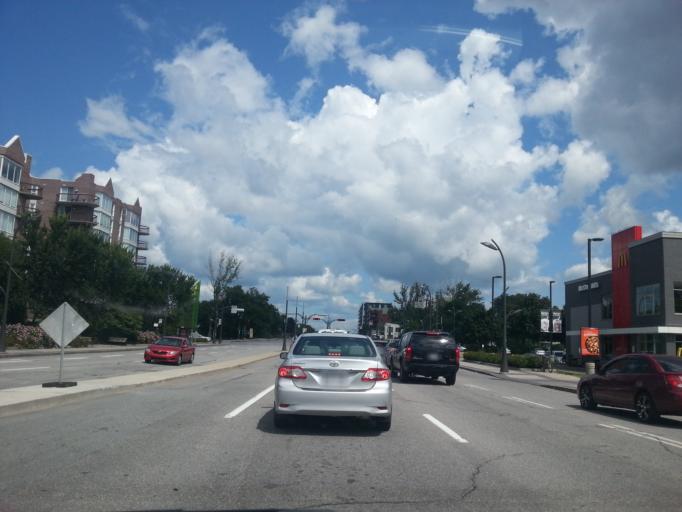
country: CA
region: Ontario
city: Ottawa
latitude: 45.4314
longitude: -75.7129
